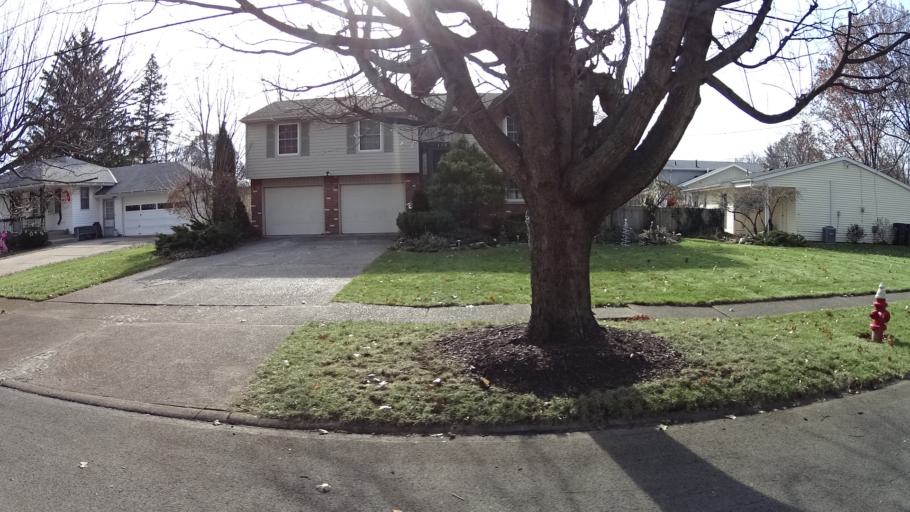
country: US
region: Ohio
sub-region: Lorain County
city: Sheffield
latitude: 41.3994
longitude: -82.0865
